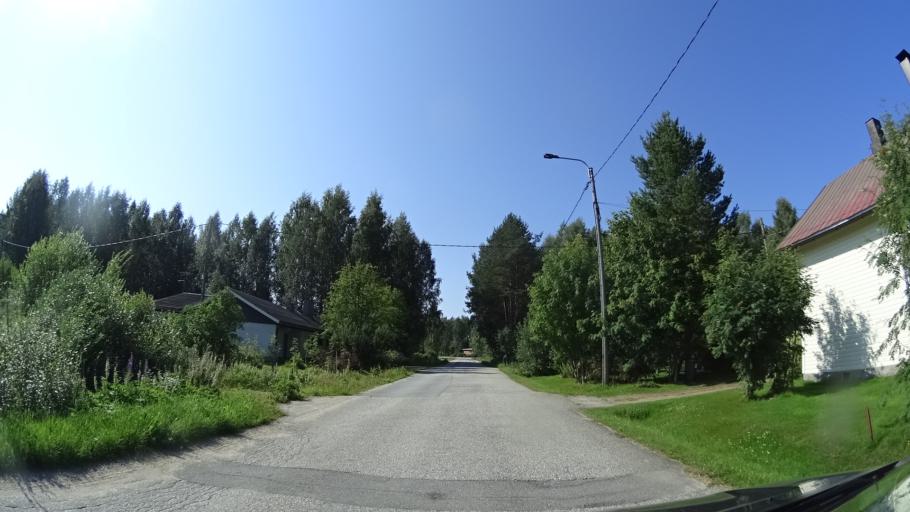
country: FI
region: North Karelia
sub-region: Joensuu
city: Juuka
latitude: 63.2382
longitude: 29.2461
